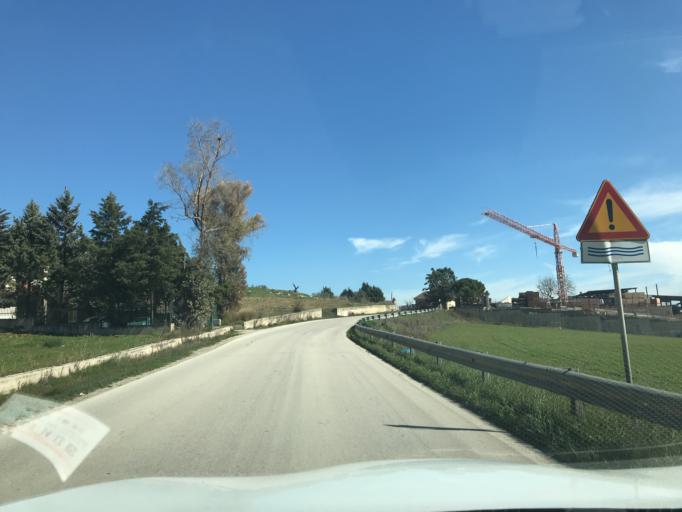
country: IT
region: Apulia
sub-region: Provincia di Bari
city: Gravina in Puglia
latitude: 40.8323
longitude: 16.4248
